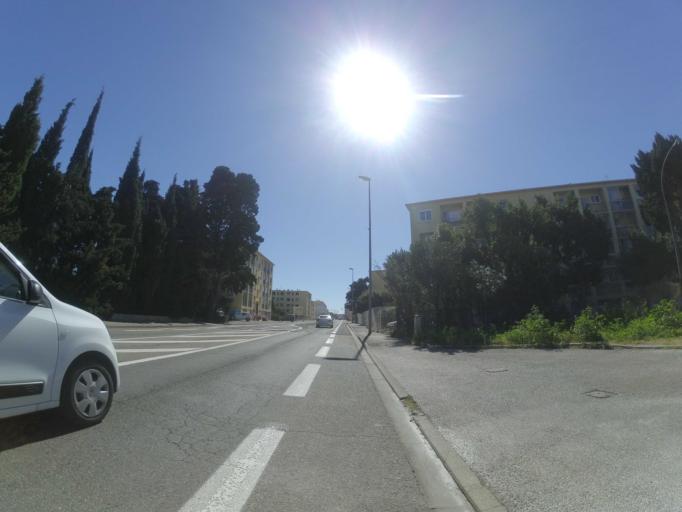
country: FR
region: Languedoc-Roussillon
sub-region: Departement des Pyrenees-Orientales
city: Perpignan
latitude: 42.7119
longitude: 2.8961
